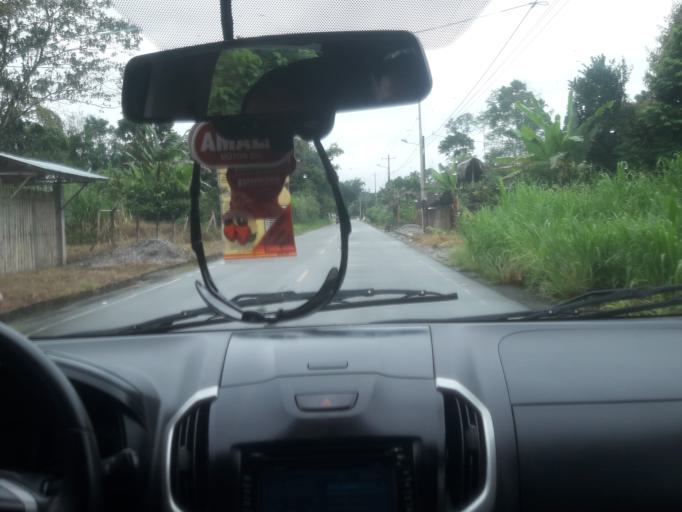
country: EC
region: Napo
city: Tena
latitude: -1.0395
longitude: -77.6937
